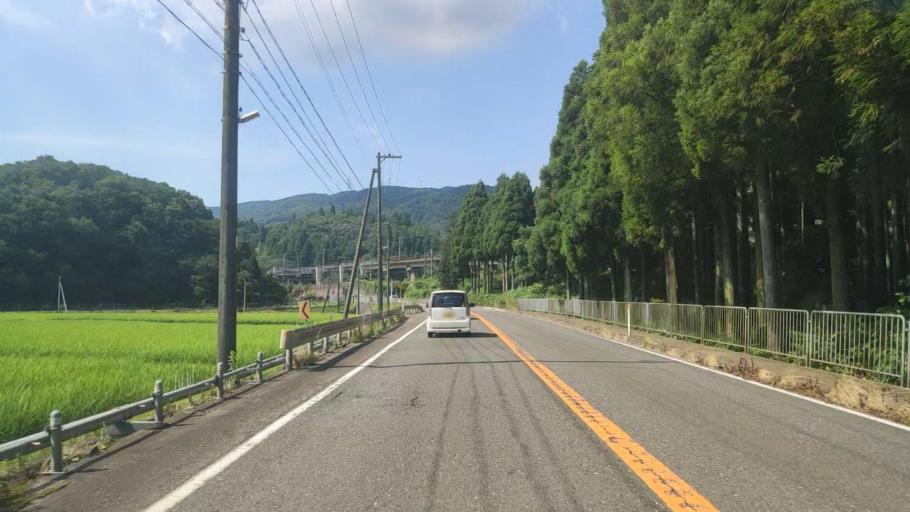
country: JP
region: Fukui
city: Tsuruga
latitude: 35.5481
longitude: 136.1477
